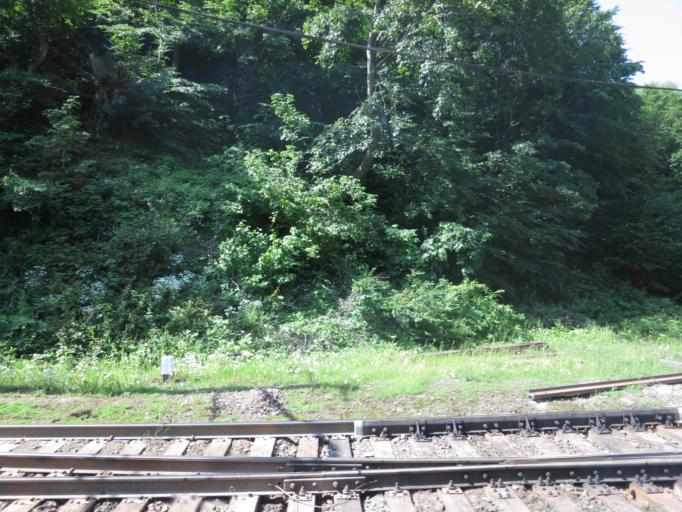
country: GE
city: Surami
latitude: 42.0032
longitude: 43.4474
